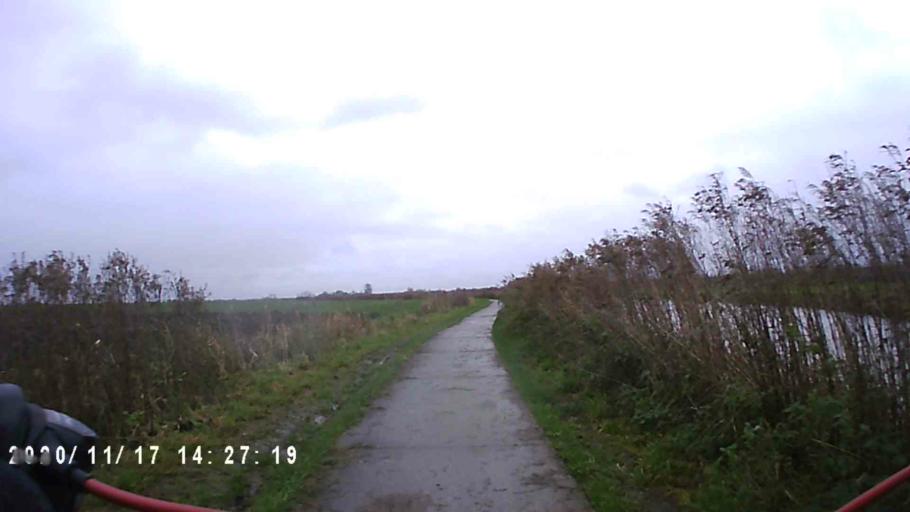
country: NL
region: Groningen
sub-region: Gemeente Zuidhorn
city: Grijpskerk
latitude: 53.2718
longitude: 6.3469
